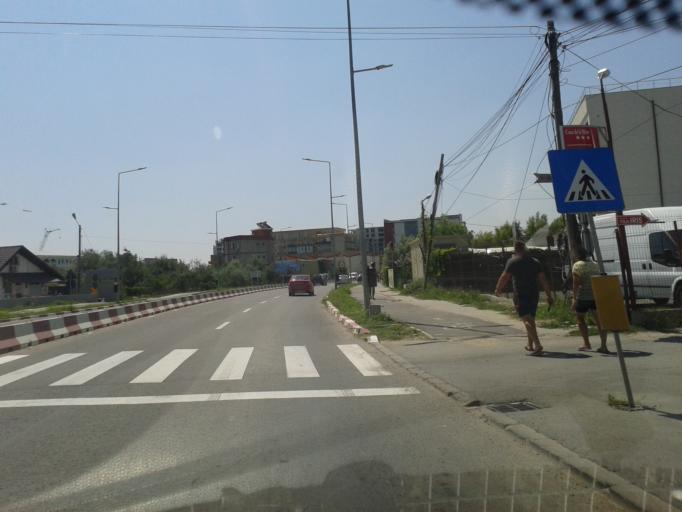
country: RO
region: Constanta
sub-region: Comuna Navodari
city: Navodari
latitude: 44.2841
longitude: 28.6181
